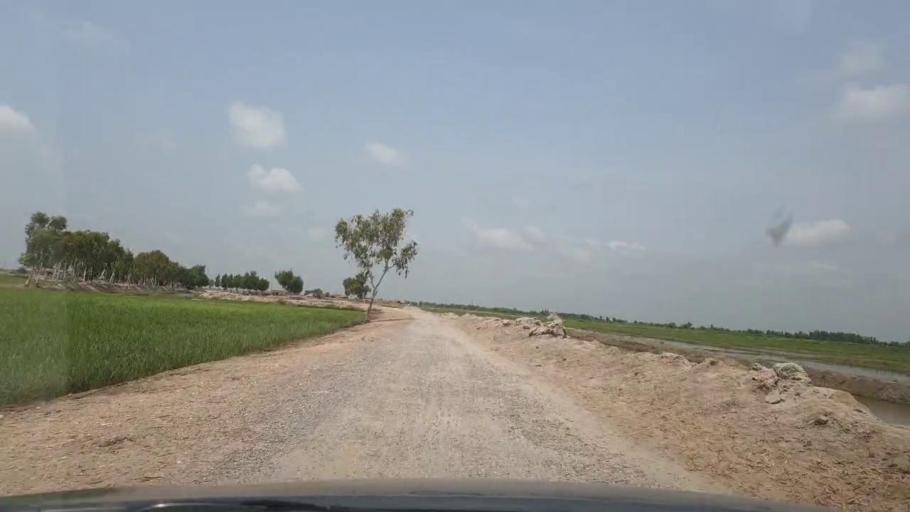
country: PK
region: Sindh
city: Ratodero
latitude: 27.9159
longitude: 68.3117
